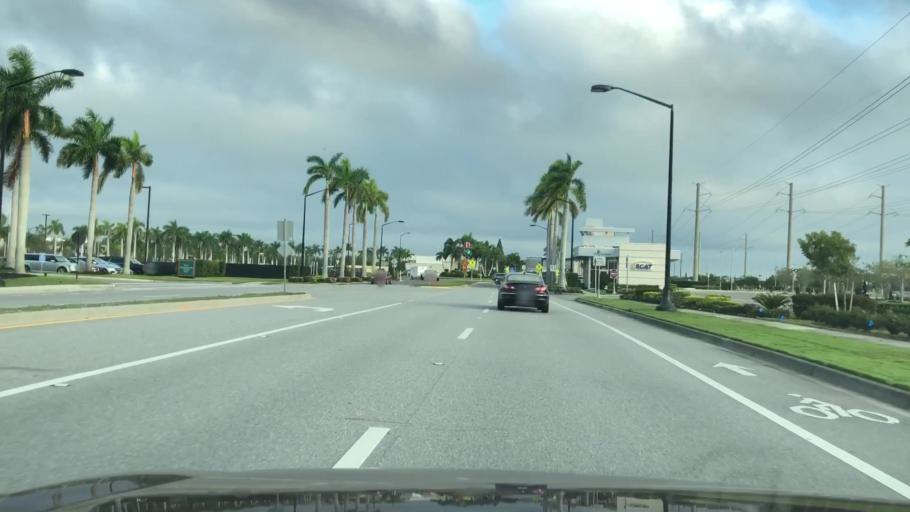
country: US
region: Florida
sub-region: Sarasota County
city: The Meadows
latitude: 27.3798
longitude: -82.4556
